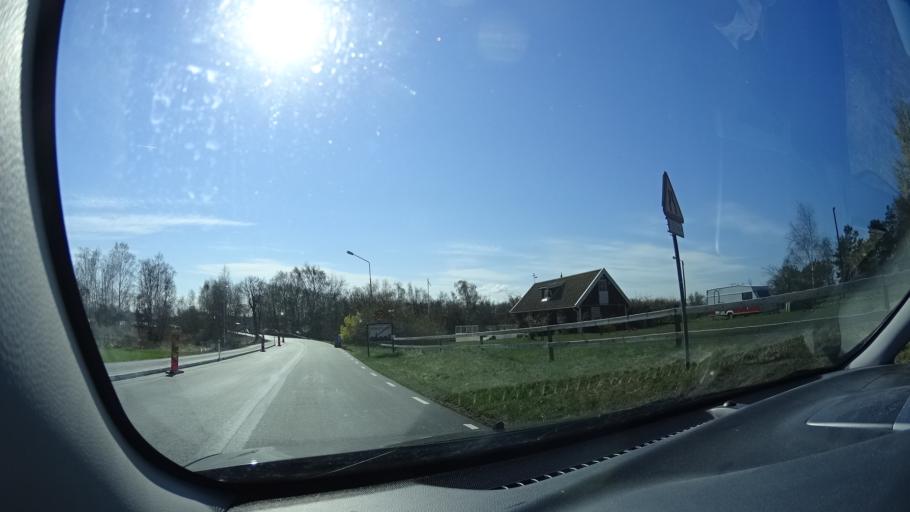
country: SE
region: Skane
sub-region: Hoganas Kommun
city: Hoganas
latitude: 56.2199
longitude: 12.6778
